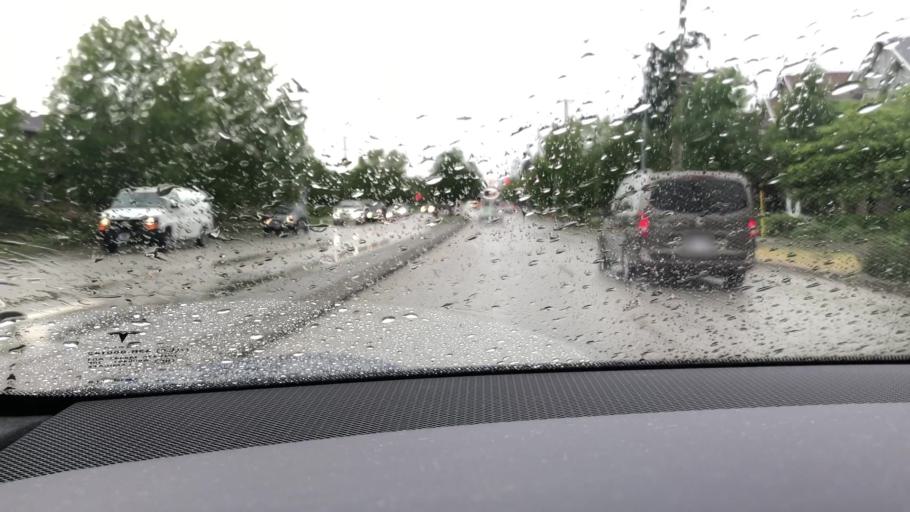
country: CA
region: British Columbia
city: Langley
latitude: 49.1335
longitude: -122.6623
